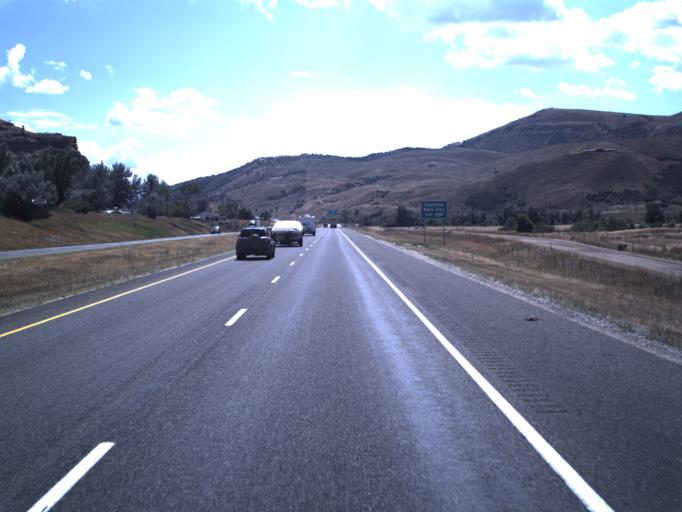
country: US
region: Utah
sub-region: Summit County
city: Coalville
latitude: 40.9805
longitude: -111.4476
